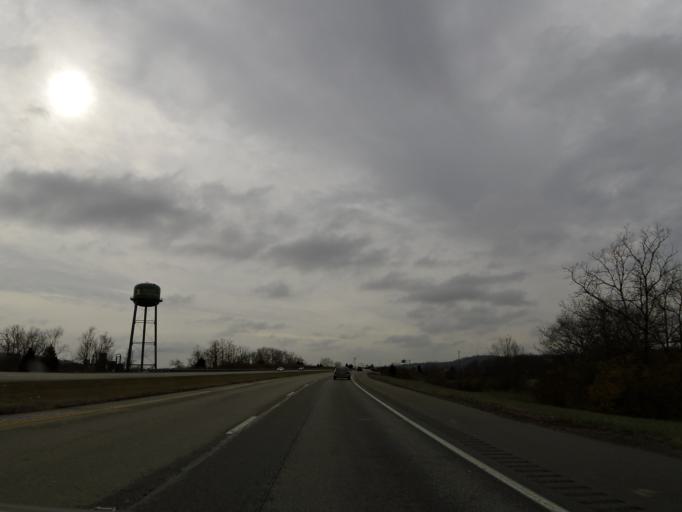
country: US
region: Ohio
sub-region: Hamilton County
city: Cleves
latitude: 39.1894
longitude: -84.7739
